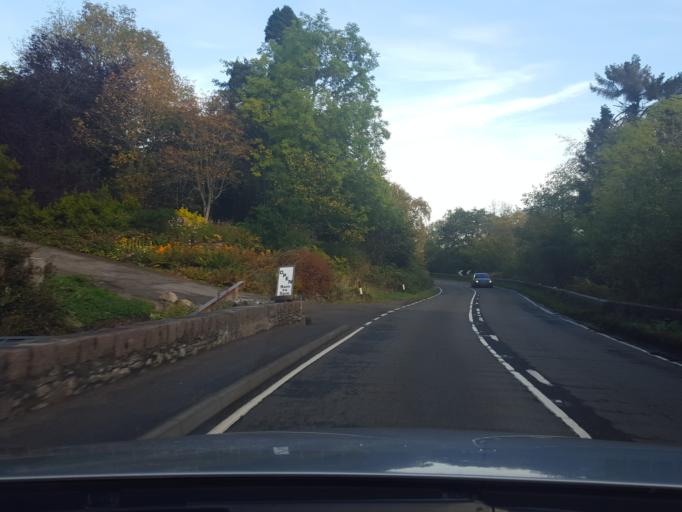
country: GB
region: Scotland
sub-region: Highland
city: Beauly
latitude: 57.3793
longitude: -4.3781
